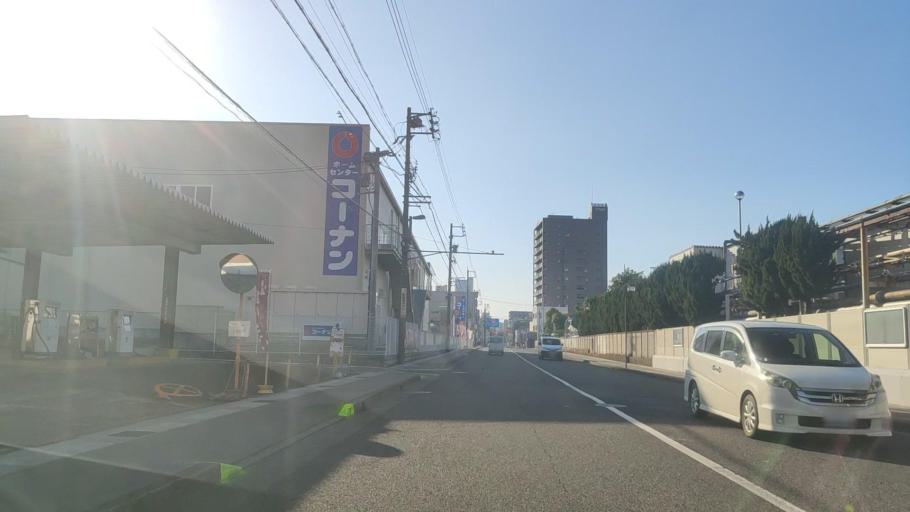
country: JP
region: Gifu
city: Gifu-shi
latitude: 35.4117
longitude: 136.7702
